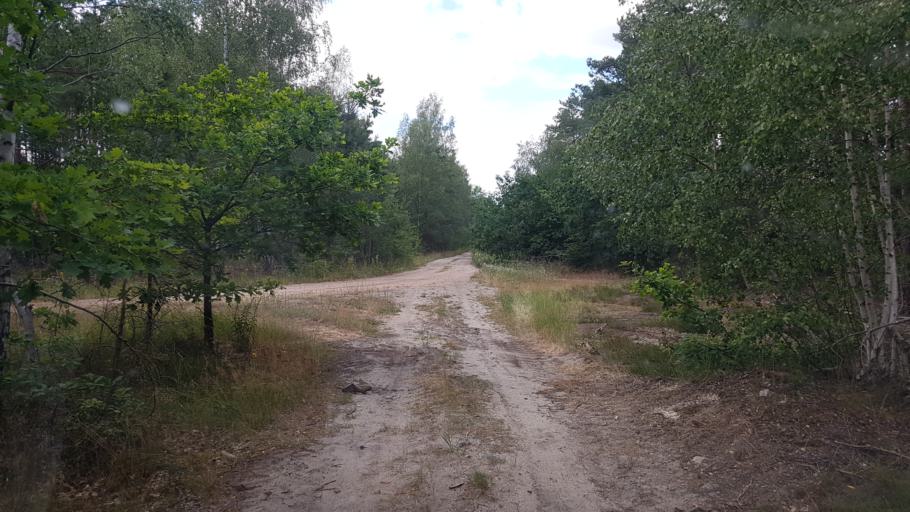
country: DE
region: Brandenburg
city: Finsterwalde
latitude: 51.6523
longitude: 13.7054
